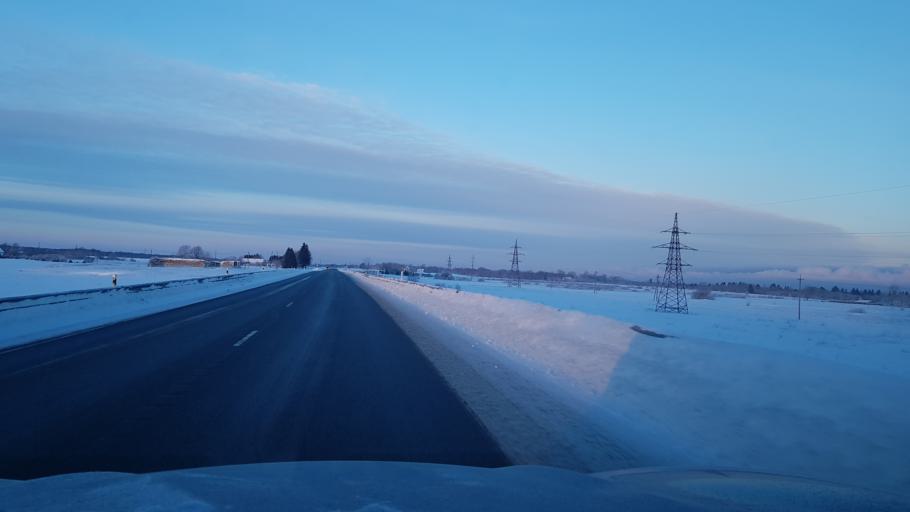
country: EE
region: Ida-Virumaa
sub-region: Narva-Joesuu linn
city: Narva-Joesuu
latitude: 59.4059
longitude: 28.0415
